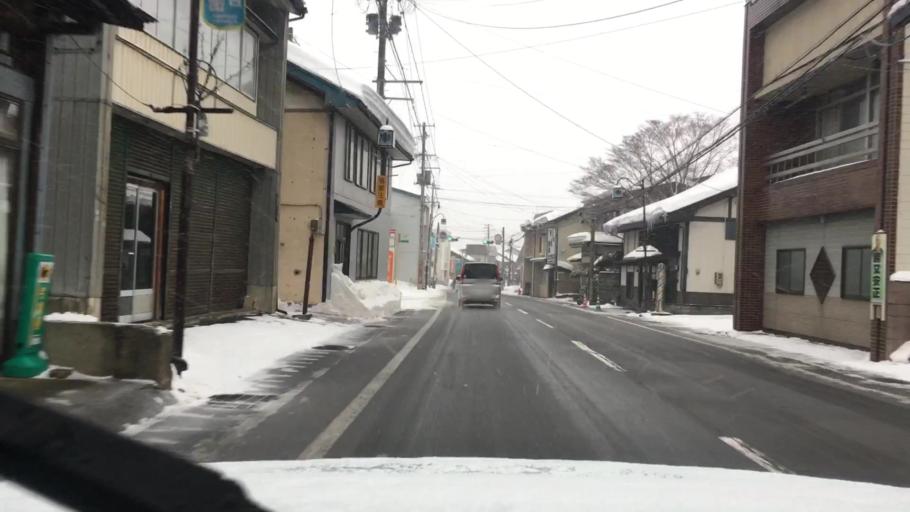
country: JP
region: Iwate
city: Ichinohe
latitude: 40.1004
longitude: 141.0482
